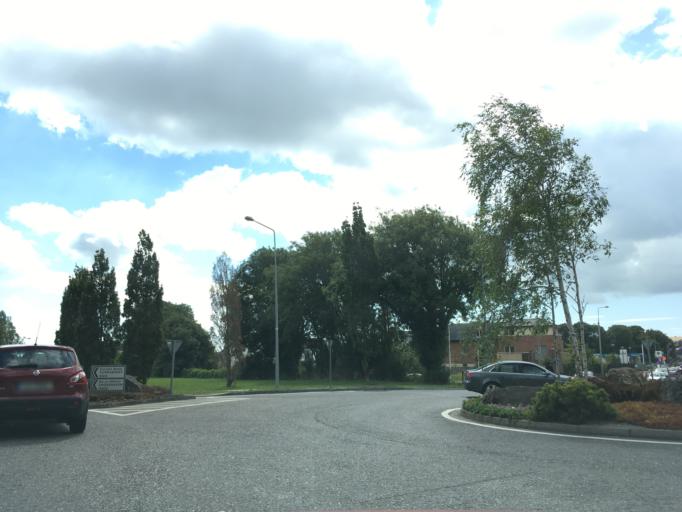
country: IE
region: Munster
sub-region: County Cork
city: Carrigaline
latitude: 51.8221
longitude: -8.3928
